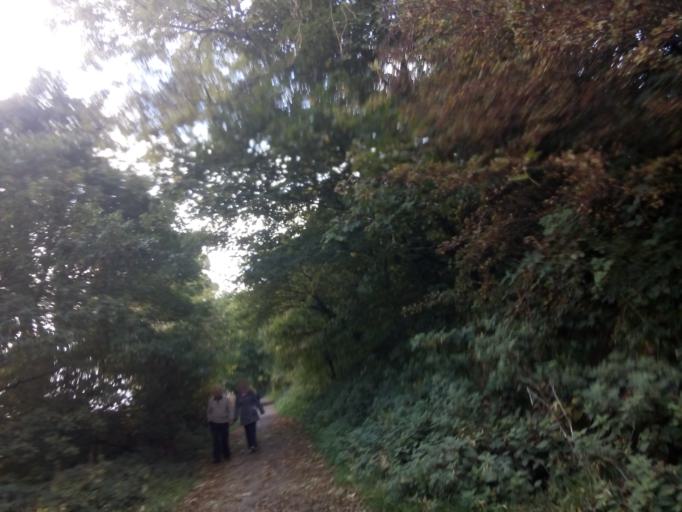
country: GB
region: England
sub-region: County Durham
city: Pittington
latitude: 54.7812
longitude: -1.5178
